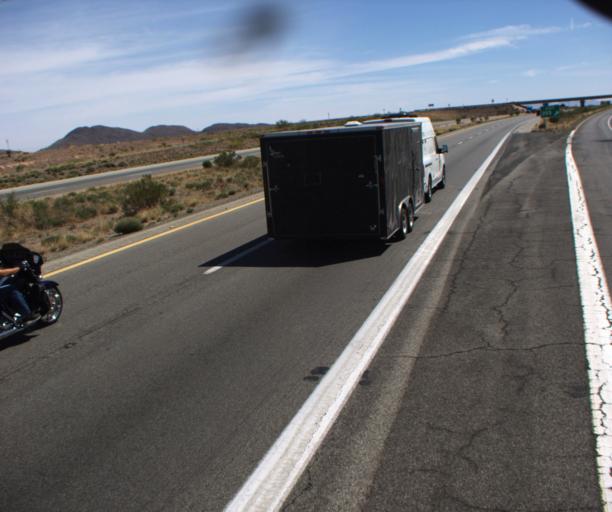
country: US
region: Arizona
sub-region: Cochise County
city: Willcox
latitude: 32.3626
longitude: -109.6254
